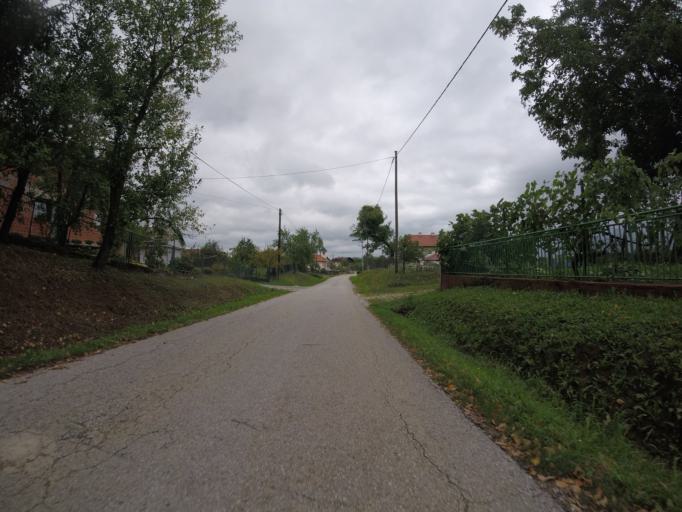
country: HR
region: Zagrebacka
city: Mraclin
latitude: 45.6028
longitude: 16.0828
